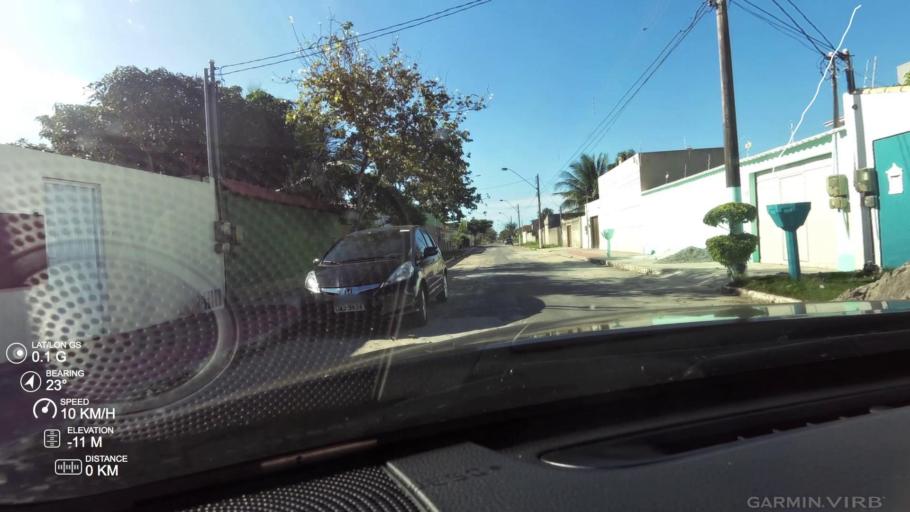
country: BR
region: Espirito Santo
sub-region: Vitoria
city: Vitoria
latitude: -20.4741
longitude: -40.3491
